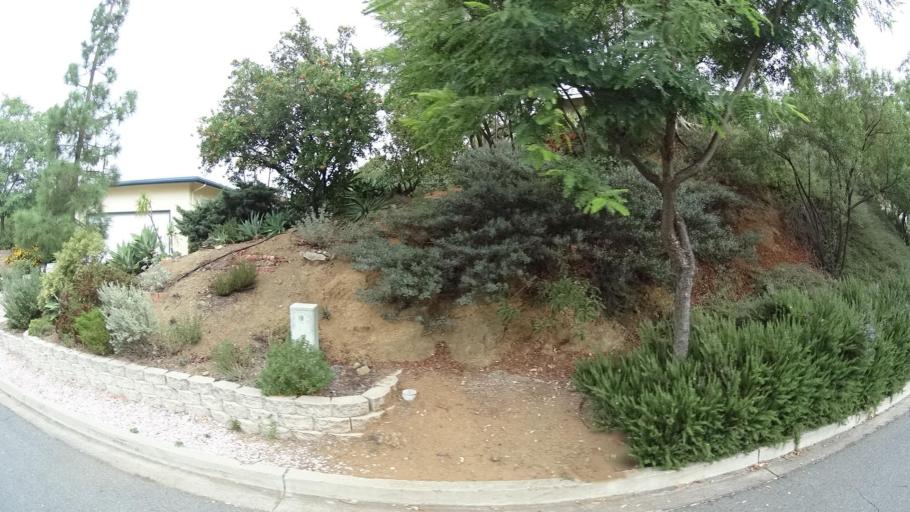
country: US
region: California
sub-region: San Diego County
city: Spring Valley
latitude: 32.7521
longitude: -116.9959
